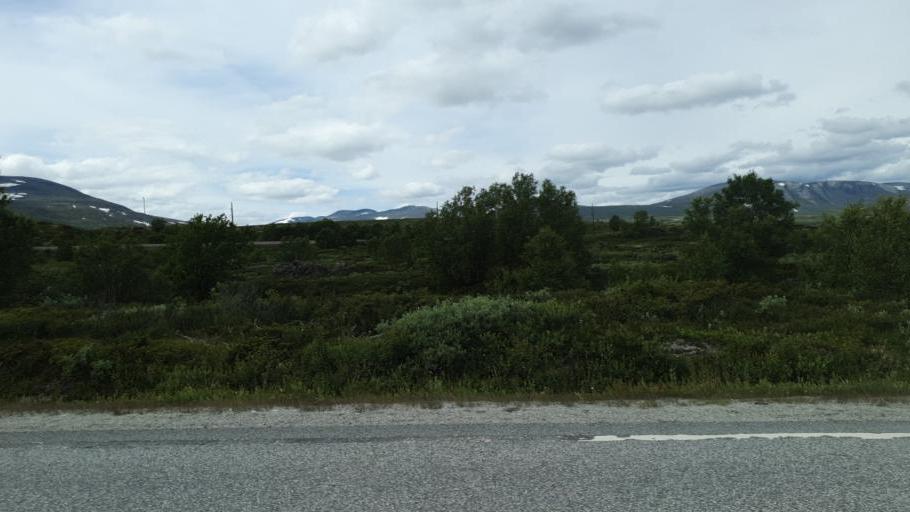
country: NO
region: Sor-Trondelag
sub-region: Oppdal
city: Oppdal
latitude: 62.2673
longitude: 9.5811
